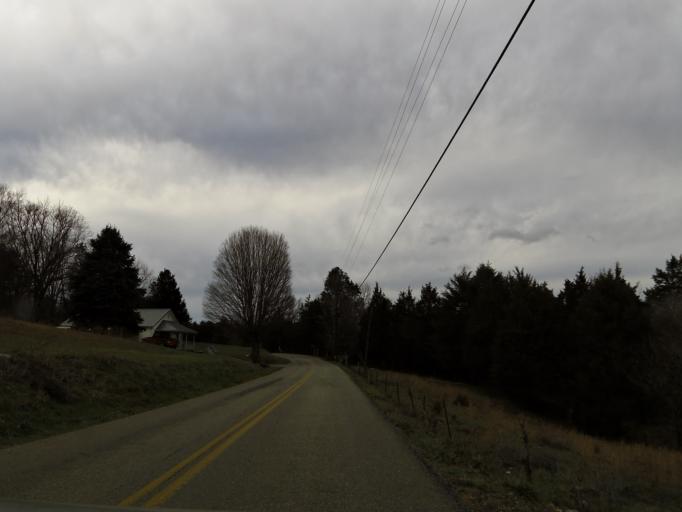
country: US
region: Tennessee
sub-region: Greene County
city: Tusculum
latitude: 36.2052
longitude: -82.7445
